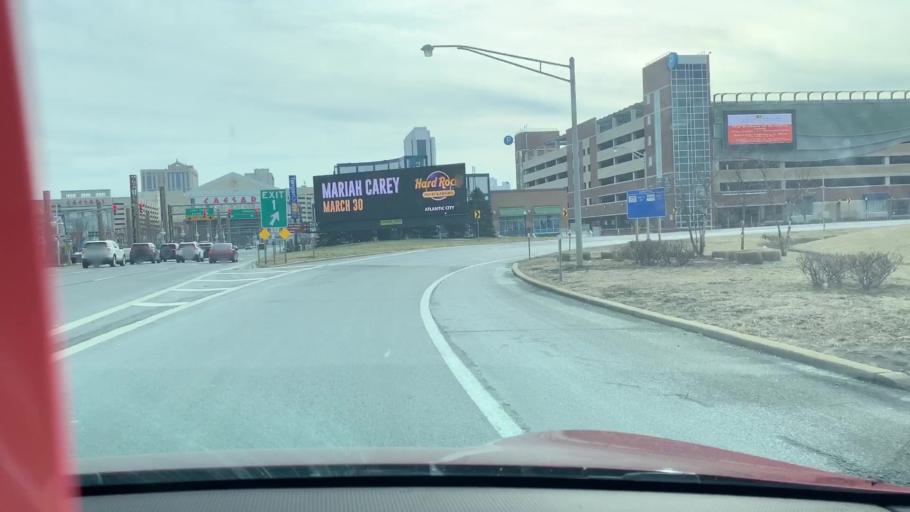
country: US
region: New Jersey
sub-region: Atlantic County
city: Atlantic City
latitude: 39.3618
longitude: -74.4402
